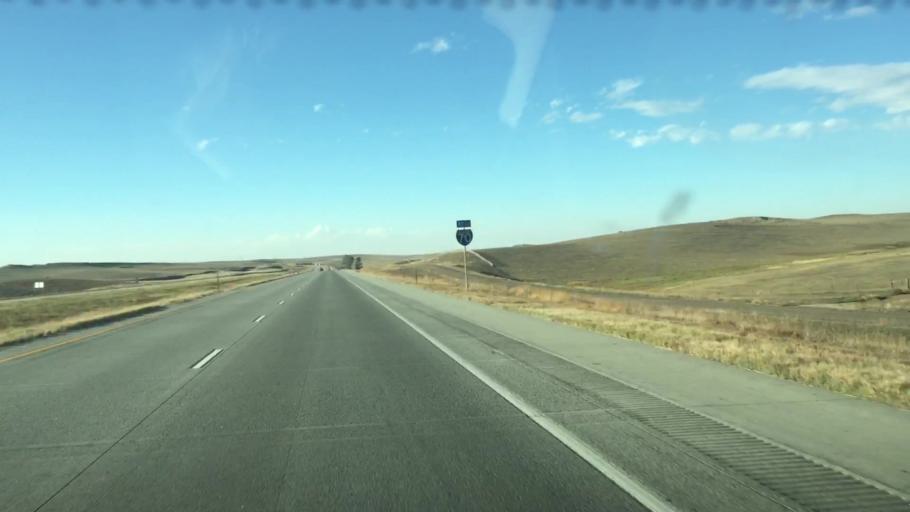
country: US
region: Colorado
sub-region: Lincoln County
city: Limon
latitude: 39.3192
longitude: -103.8293
